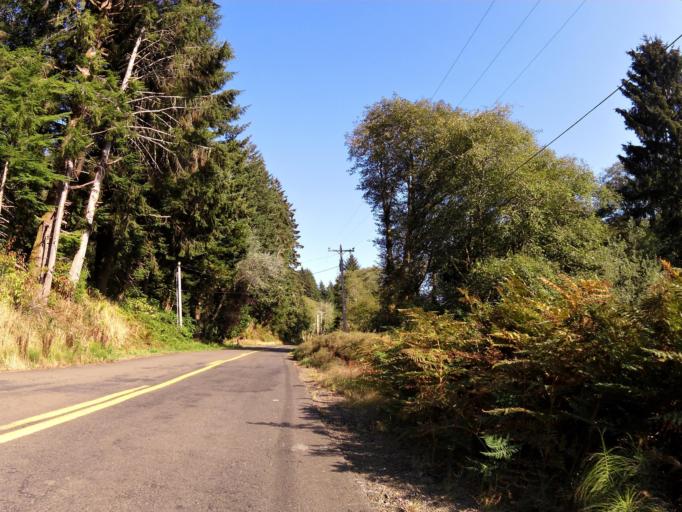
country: US
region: Oregon
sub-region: Lincoln County
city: Rose Lodge
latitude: 45.0749
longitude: -123.9291
